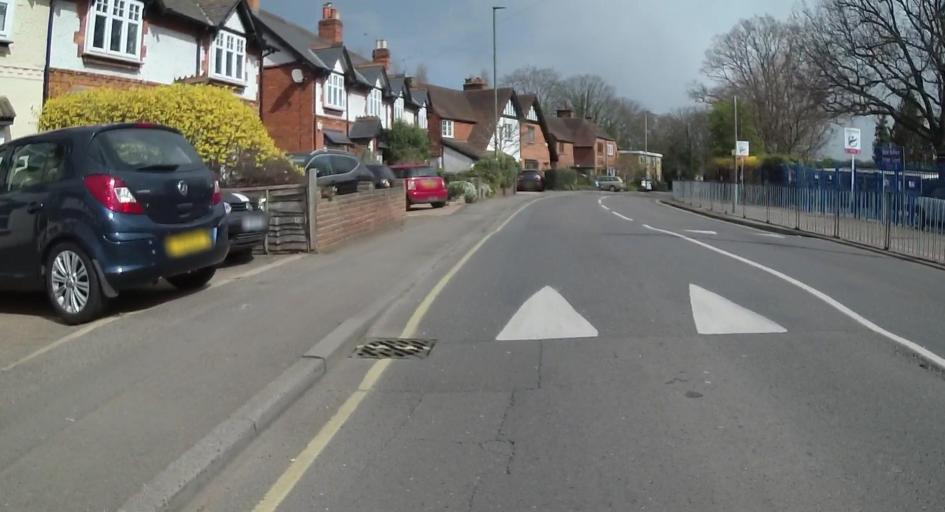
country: GB
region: England
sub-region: Surrey
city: West Byfleet
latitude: 51.3404
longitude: -0.5013
